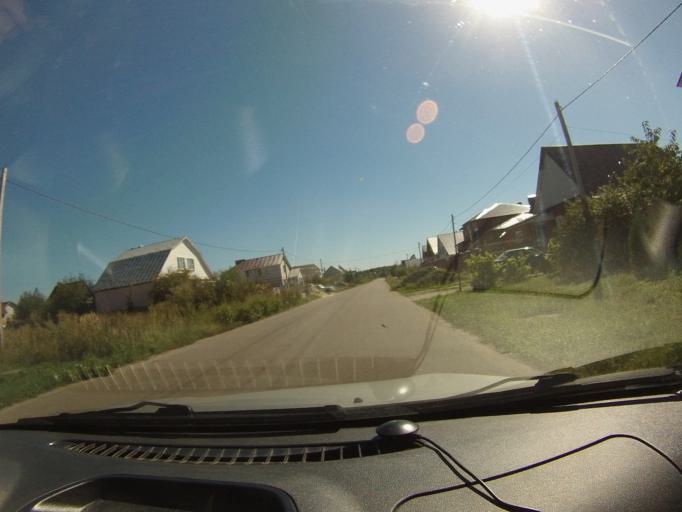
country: RU
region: Tambov
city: Komsomolets
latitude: 52.7658
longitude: 41.3628
